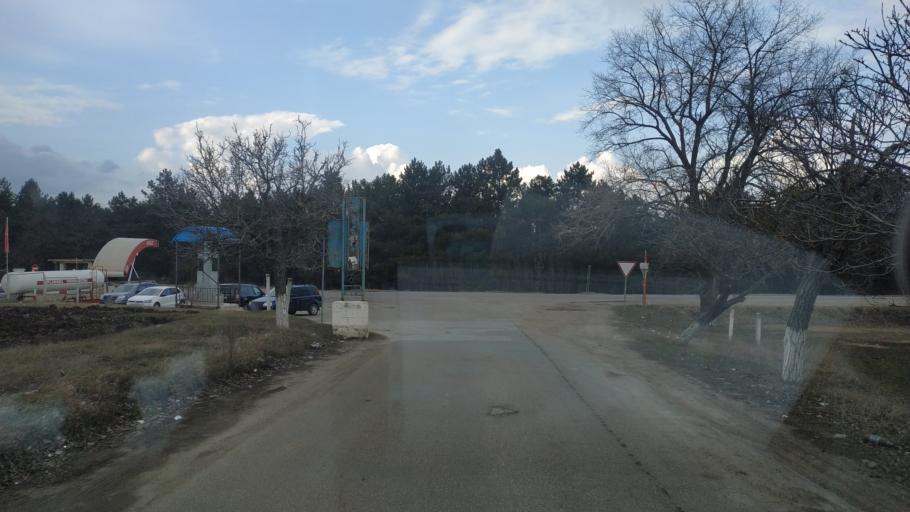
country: MD
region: Anenii Noi
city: Anenii Noi
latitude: 46.8560
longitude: 29.3484
